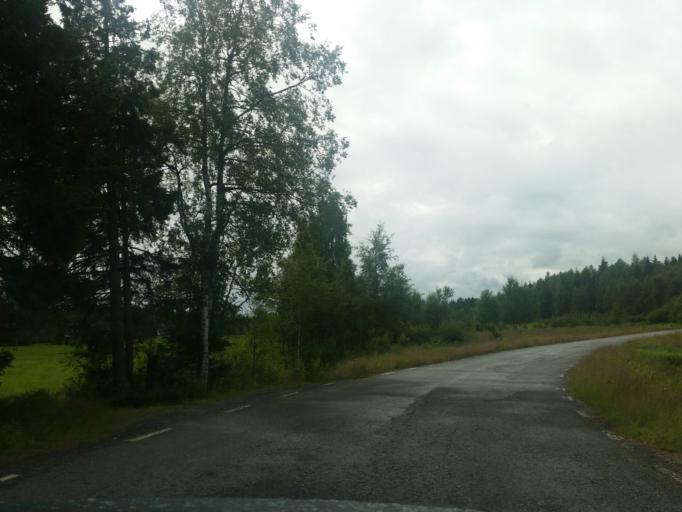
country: SE
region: Vaesterbotten
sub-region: Robertsfors Kommun
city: Robertsfors
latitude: 64.0324
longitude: 20.8443
